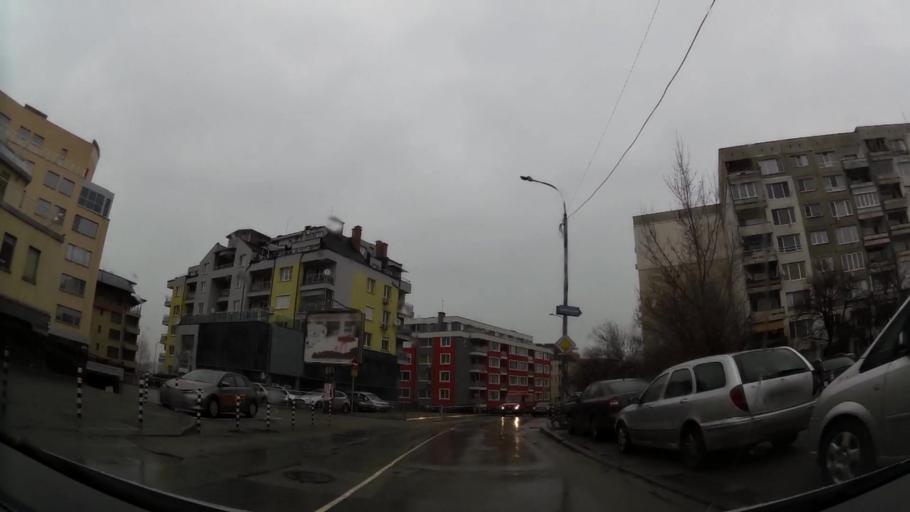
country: BG
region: Sofia-Capital
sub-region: Stolichna Obshtina
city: Sofia
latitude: 42.6435
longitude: 23.3666
